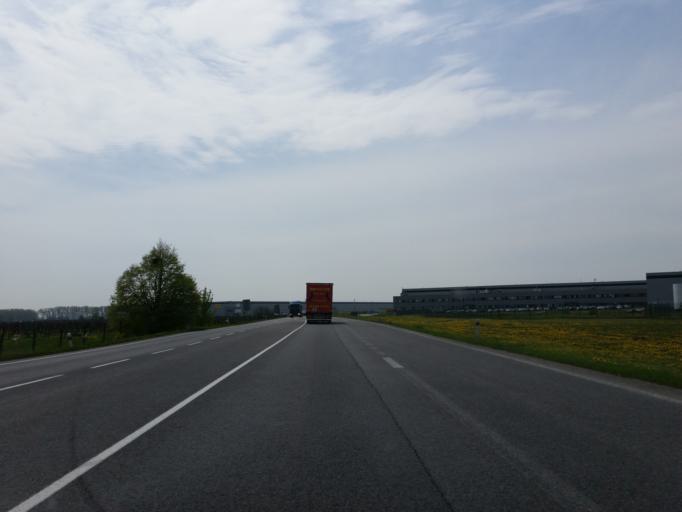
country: SK
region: Trnavsky
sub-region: Okres Galanta
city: Galanta
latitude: 48.2378
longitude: 17.7324
